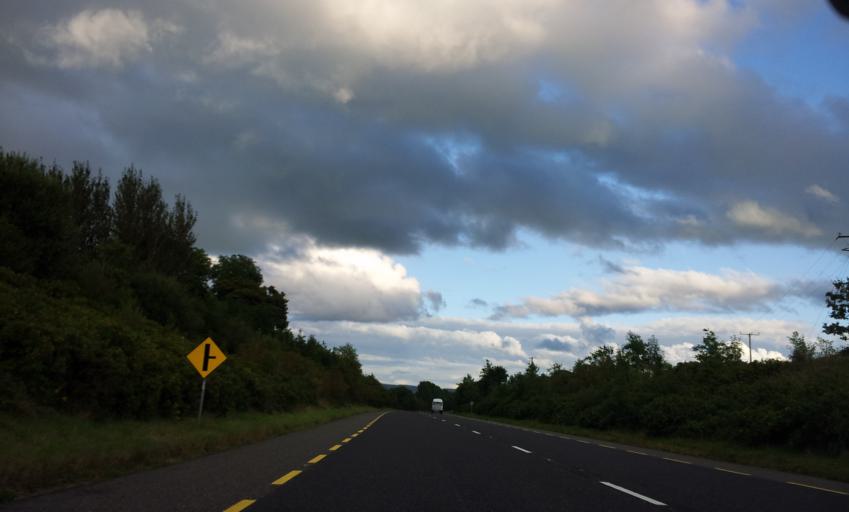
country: IE
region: Munster
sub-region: Ciarrai
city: Castleisland
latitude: 52.2422
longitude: -9.5109
